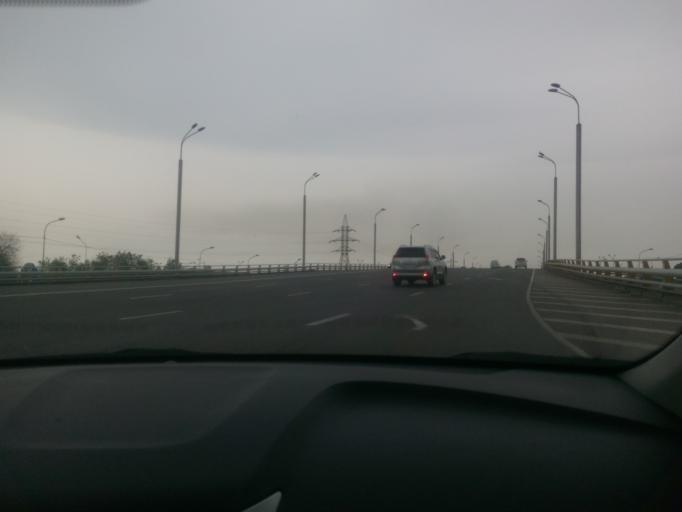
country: KZ
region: Almaty Qalasy
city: Almaty
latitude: 43.2419
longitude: 76.8284
